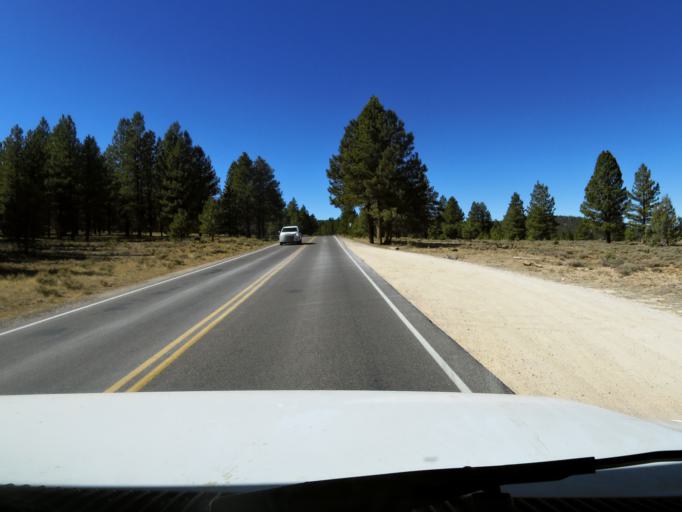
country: US
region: Utah
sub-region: Garfield County
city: Panguitch
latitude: 37.6070
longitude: -112.1913
